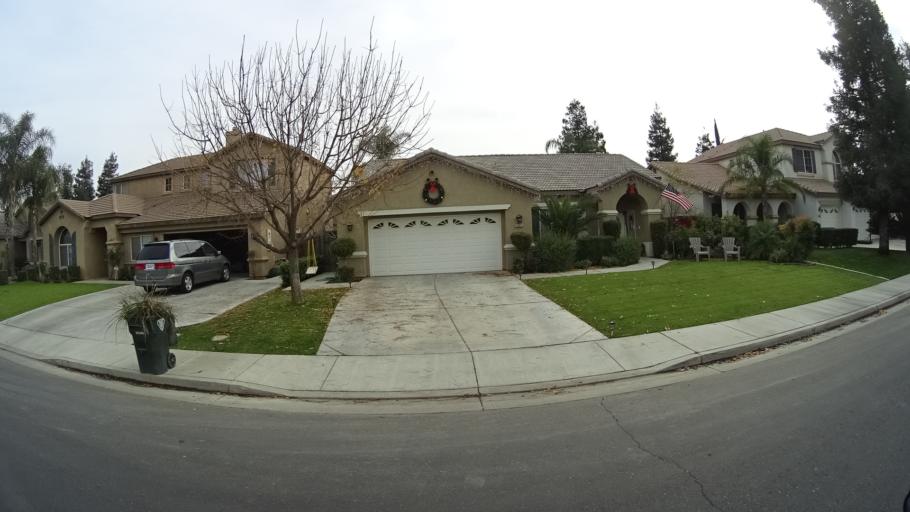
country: US
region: California
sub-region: Kern County
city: Rosedale
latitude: 35.3420
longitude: -119.1359
